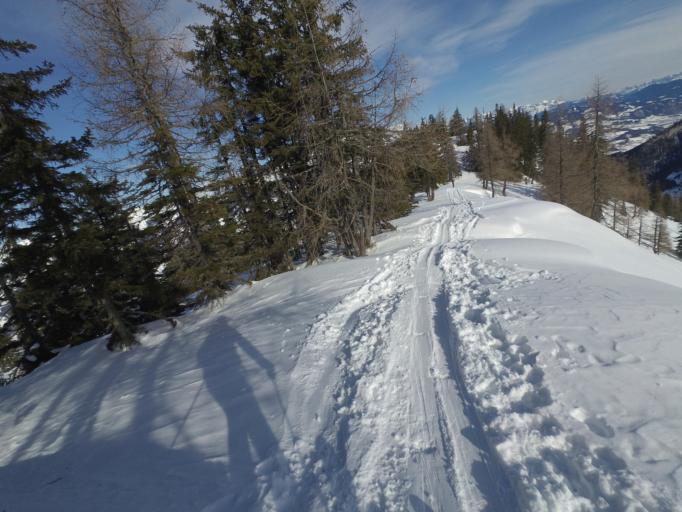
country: AT
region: Salzburg
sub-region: Politischer Bezirk Zell am See
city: Rauris
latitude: 47.2649
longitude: 13.0187
